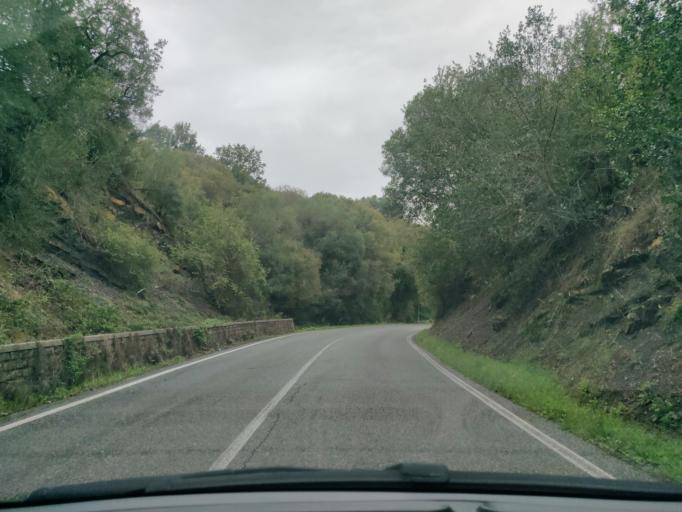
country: IT
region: Latium
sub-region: Citta metropolitana di Roma Capitale
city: Allumiere
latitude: 42.1414
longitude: 11.8776
